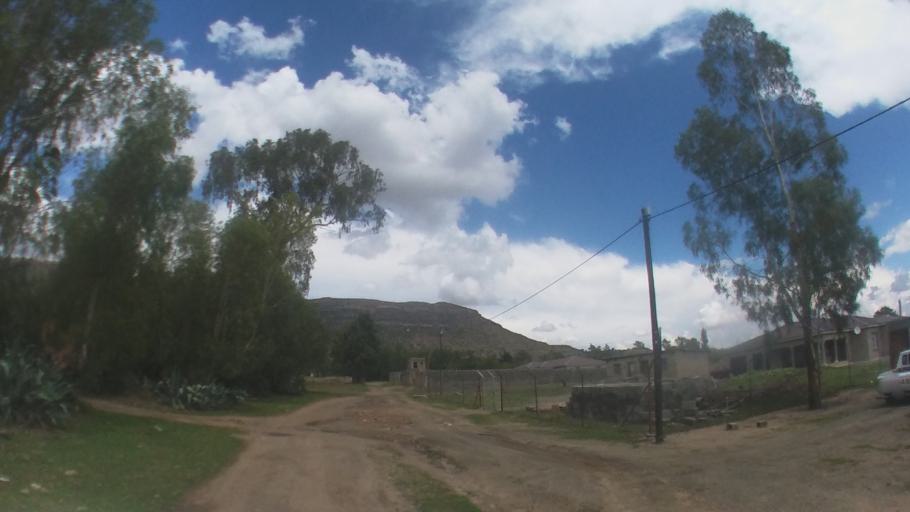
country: LS
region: Maseru
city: Nako
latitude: -29.6205
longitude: 27.5052
